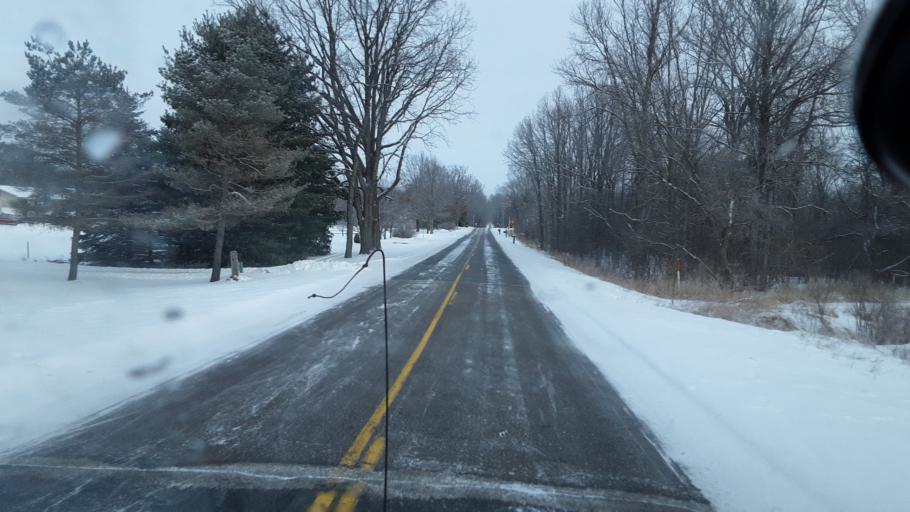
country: US
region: Michigan
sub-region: Jackson County
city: Jackson
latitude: 42.3275
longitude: -84.4828
